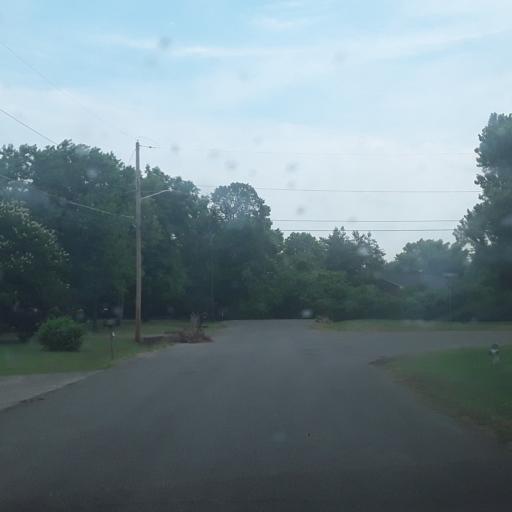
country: US
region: Tennessee
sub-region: Williamson County
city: Brentwood Estates
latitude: 36.0547
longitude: -86.7179
